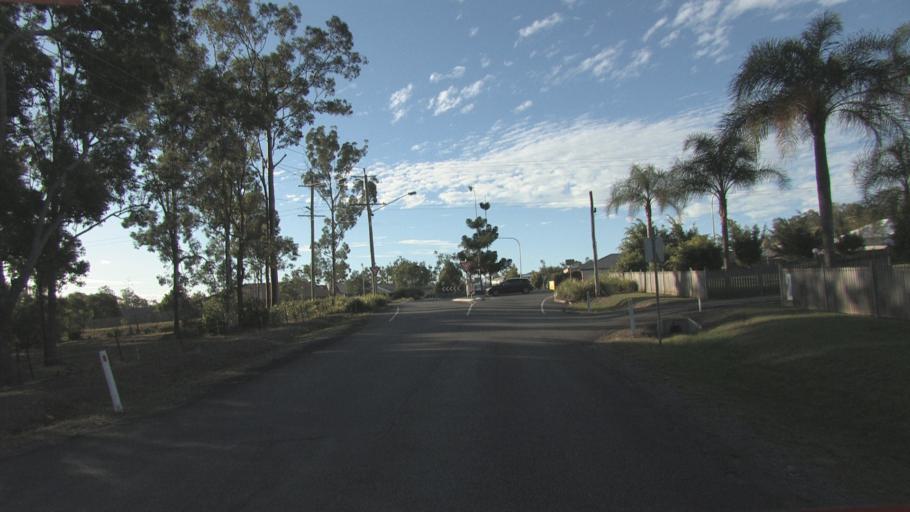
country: AU
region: Queensland
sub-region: Logan
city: Waterford West
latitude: -27.7205
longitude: 153.1541
